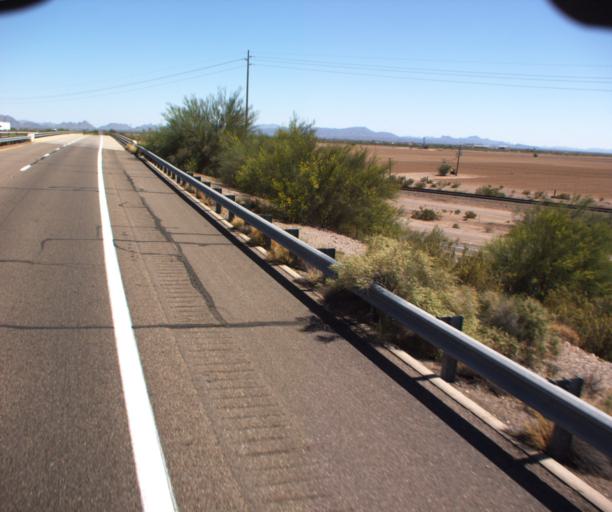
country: US
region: Arizona
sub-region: Maricopa County
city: Gila Bend
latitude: 32.9424
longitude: -112.7430
